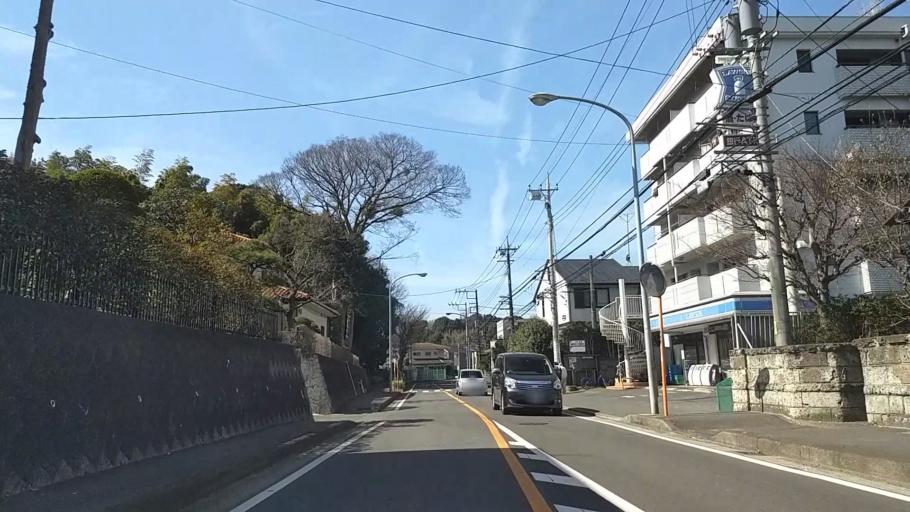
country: JP
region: Kanagawa
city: Fujisawa
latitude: 35.3906
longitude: 139.5128
